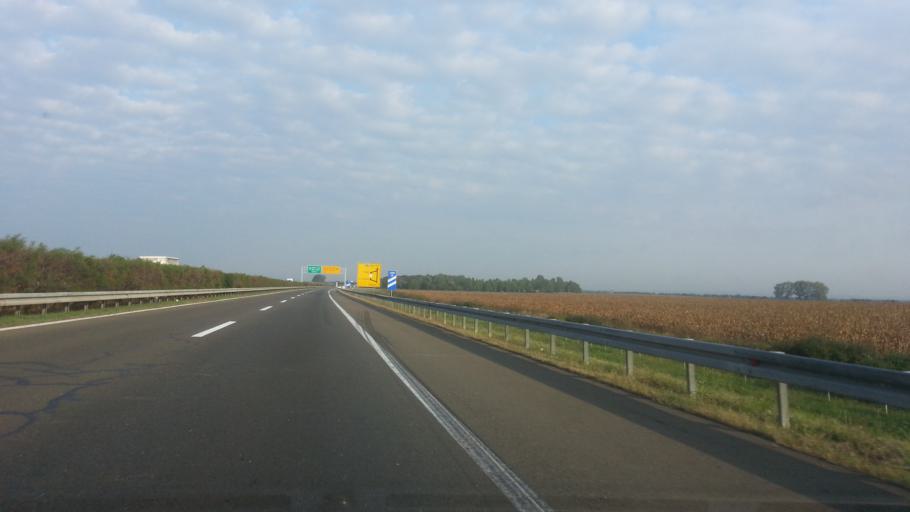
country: RS
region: Autonomna Pokrajina Vojvodina
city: Nova Pazova
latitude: 44.9793
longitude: 20.2227
